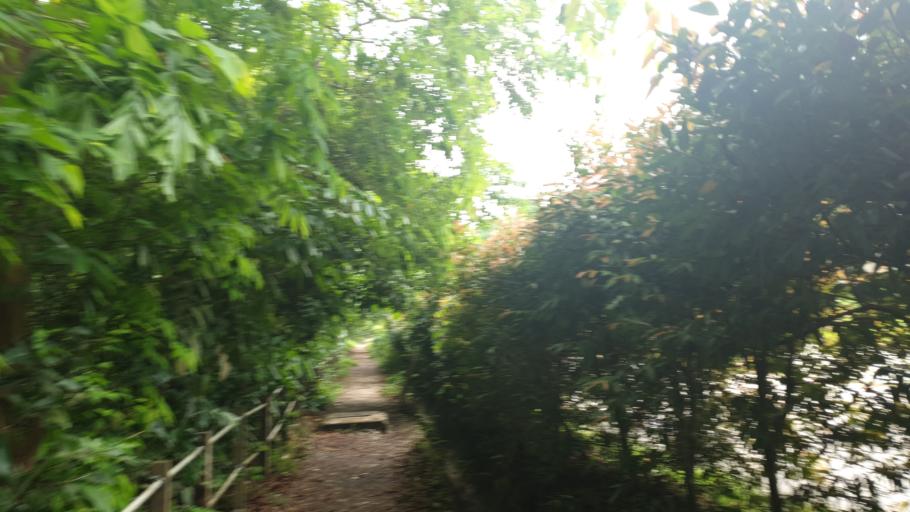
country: SG
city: Singapore
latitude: 1.3582
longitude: 103.8195
